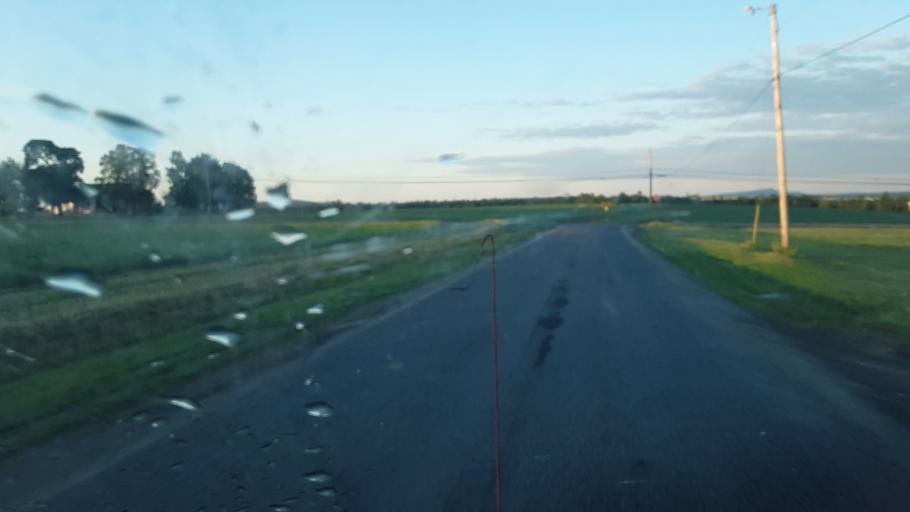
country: US
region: Maine
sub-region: Aroostook County
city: Caribou
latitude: 46.8036
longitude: -68.1349
